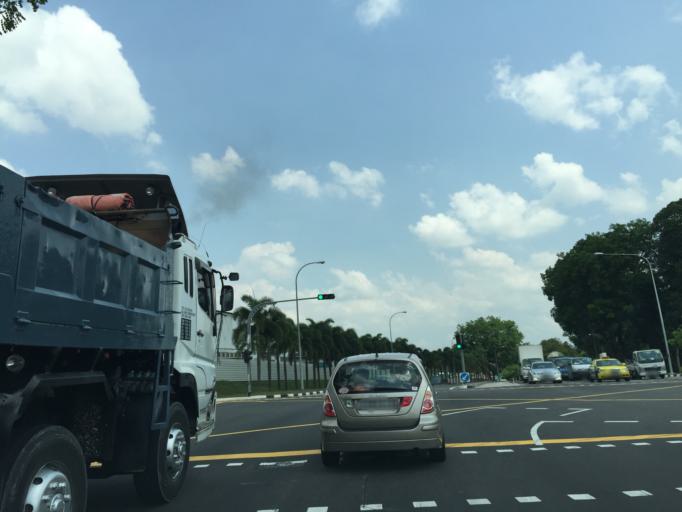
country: MY
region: Johor
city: Johor Bahru
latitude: 1.4287
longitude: 103.7663
